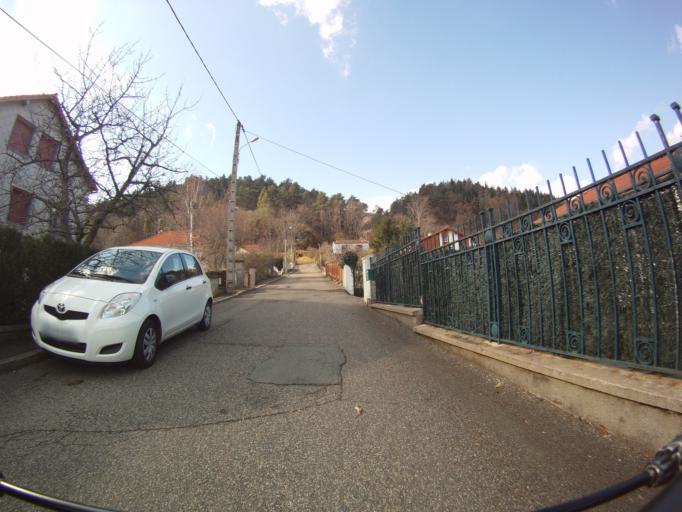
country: FR
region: Auvergne
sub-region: Departement du Puy-de-Dome
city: Ceyrat
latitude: 45.7375
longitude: 3.0584
